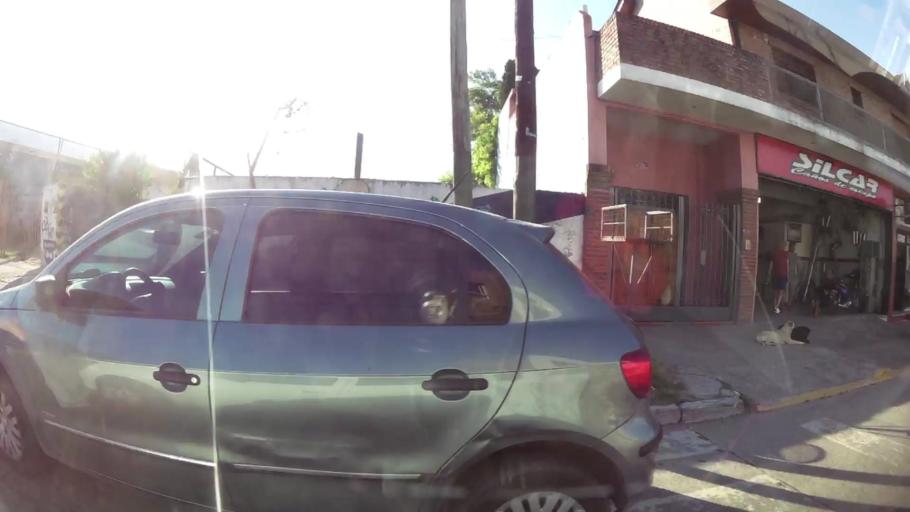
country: AR
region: Buenos Aires
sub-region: Partido de Merlo
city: Merlo
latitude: -34.6779
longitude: -58.7268
